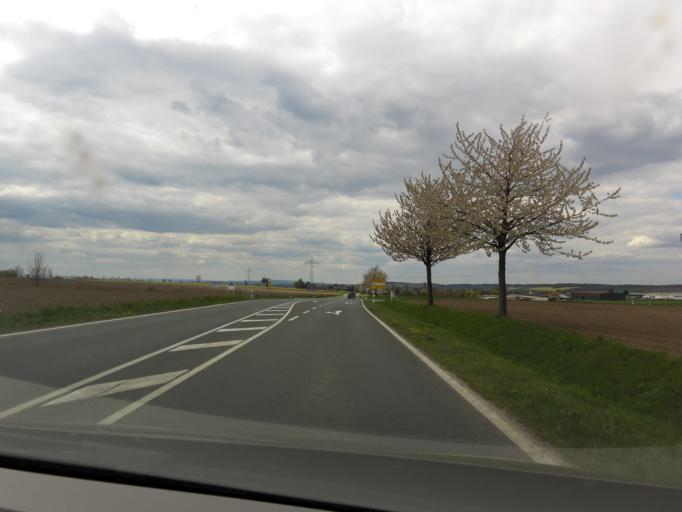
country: DE
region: Thuringia
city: Grossheringen
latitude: 51.1282
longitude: 11.6726
